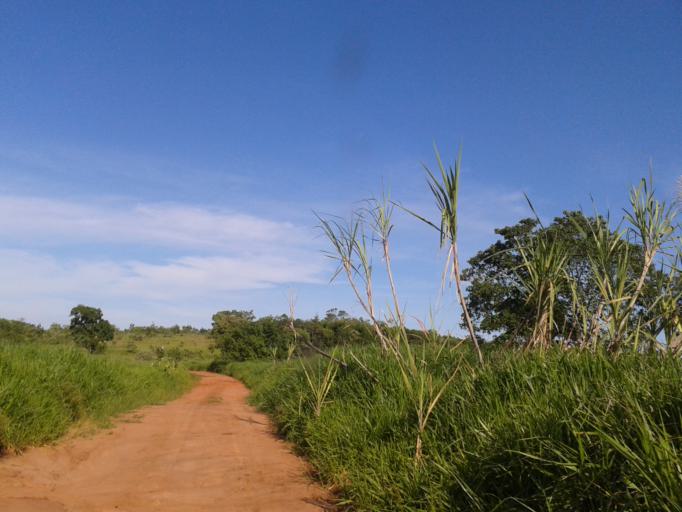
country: BR
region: Minas Gerais
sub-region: Santa Vitoria
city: Santa Vitoria
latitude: -19.1205
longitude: -50.0002
